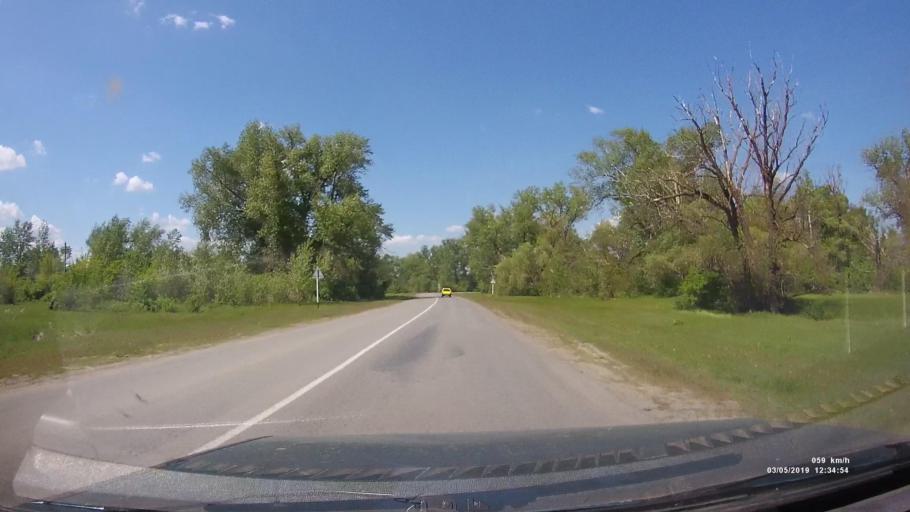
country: RU
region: Rostov
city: Semikarakorsk
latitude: 47.5235
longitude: 40.7642
